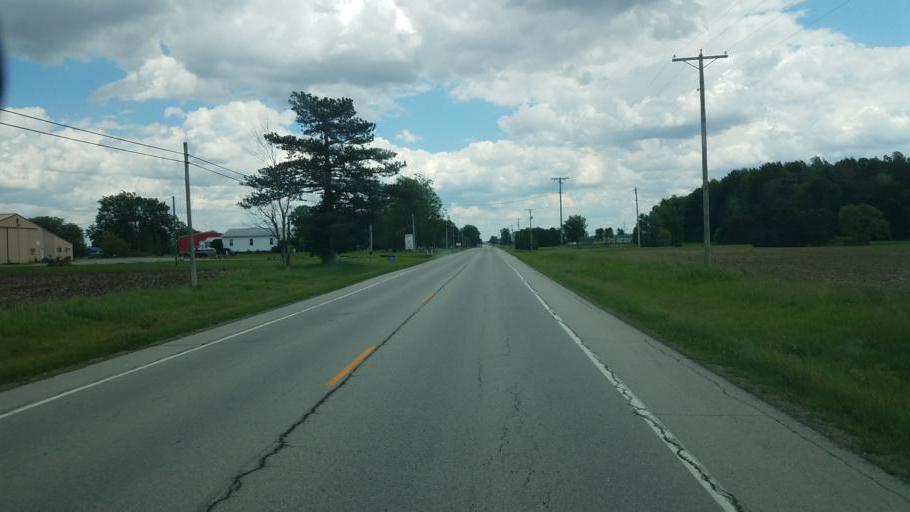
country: US
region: Ohio
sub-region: Crawford County
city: Bucyrus
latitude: 40.8365
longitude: -83.0701
